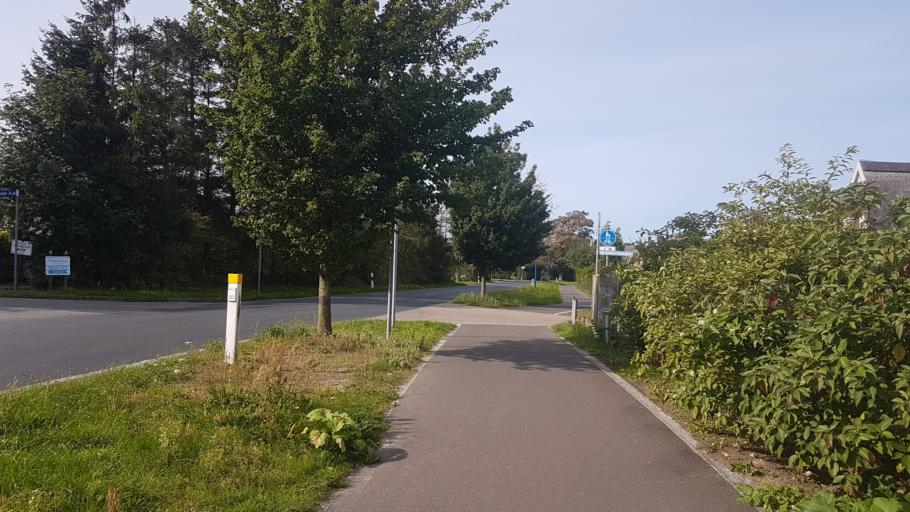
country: DE
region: Mecklenburg-Vorpommern
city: Gingst
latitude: 54.4521
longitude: 13.1821
